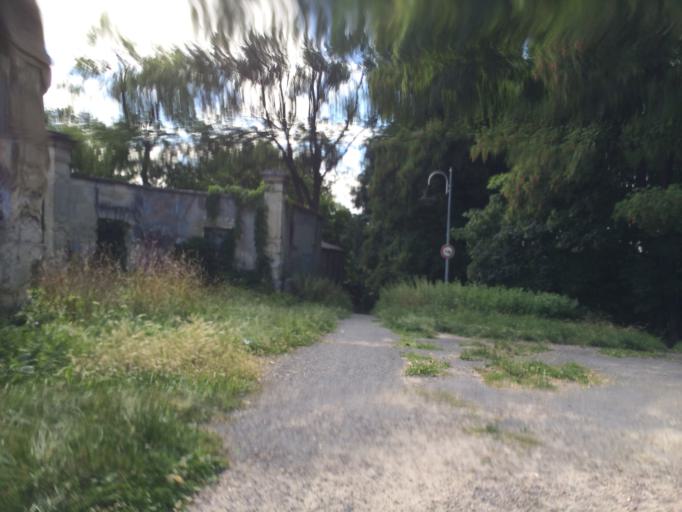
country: FR
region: Ile-de-France
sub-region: Departement de l'Essonne
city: Saulx-les-Chartreux
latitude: 48.6905
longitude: 2.2751
